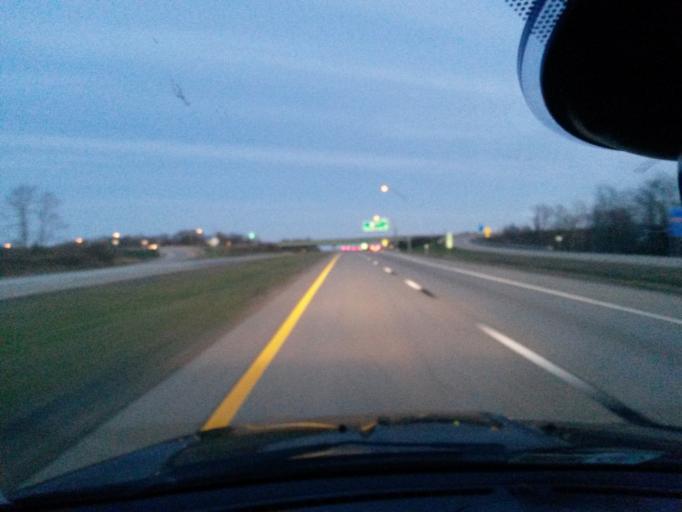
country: US
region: West Virginia
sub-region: Raleigh County
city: Daniels
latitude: 37.7734
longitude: -81.0700
